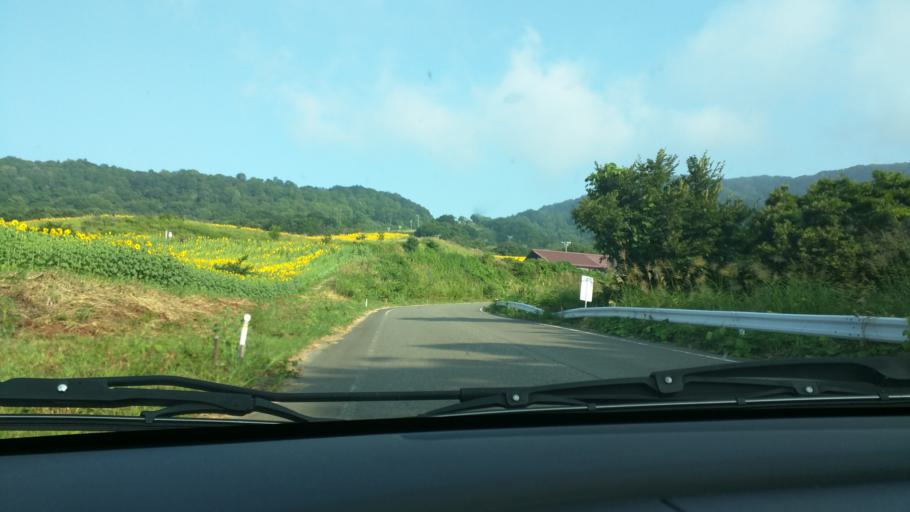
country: JP
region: Fukushima
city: Kitakata
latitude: 37.7476
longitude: 139.8684
